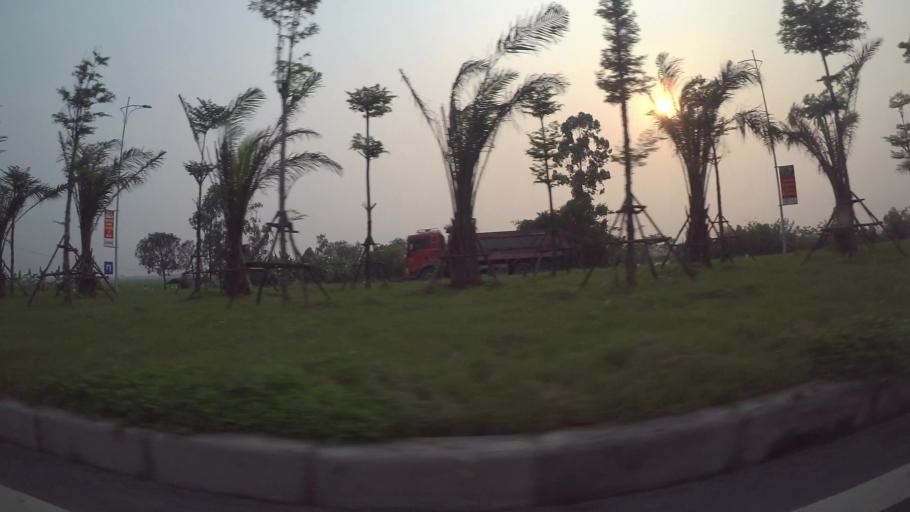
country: VN
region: Ha Noi
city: Kim Bai
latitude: 20.8831
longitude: 105.7985
